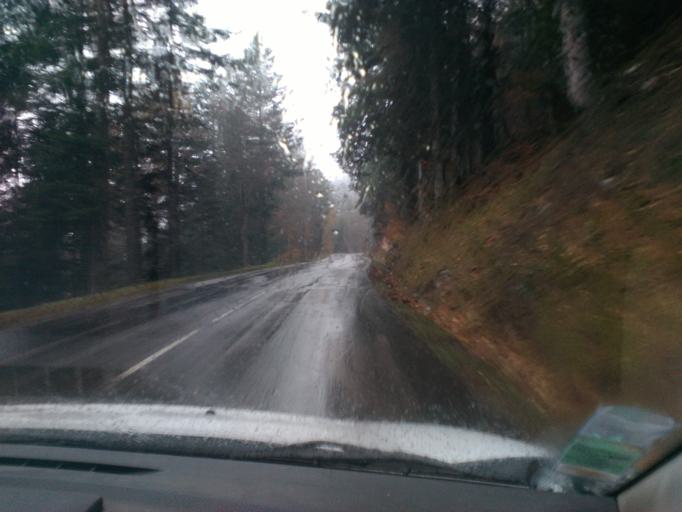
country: FR
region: Lorraine
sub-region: Departement des Vosges
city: Xonrupt-Longemer
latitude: 48.0665
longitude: 6.9687
